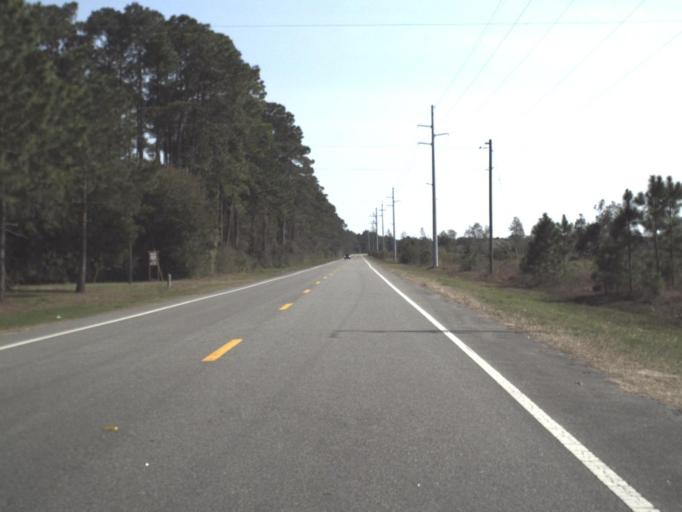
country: US
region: Florida
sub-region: Franklin County
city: Carrabelle
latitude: 29.9494
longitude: -84.5031
